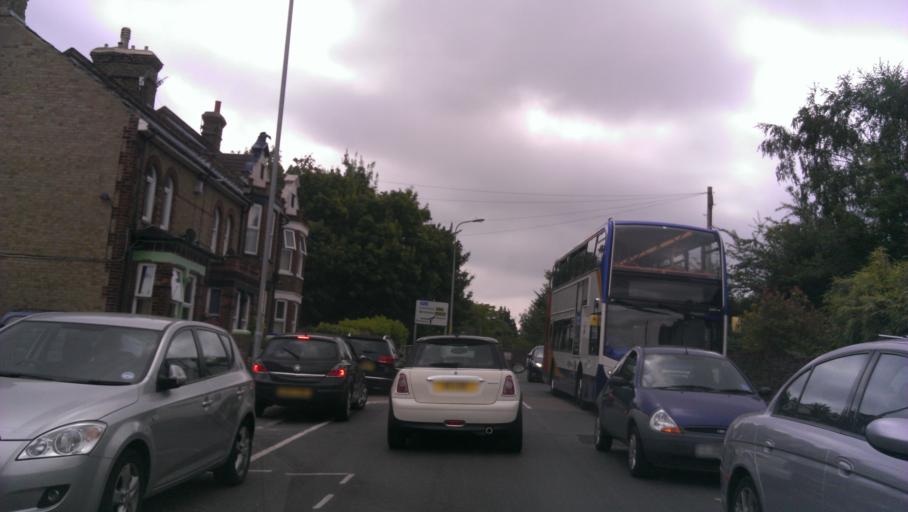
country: GB
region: England
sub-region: Kent
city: Faversham
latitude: 51.3127
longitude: 0.9049
